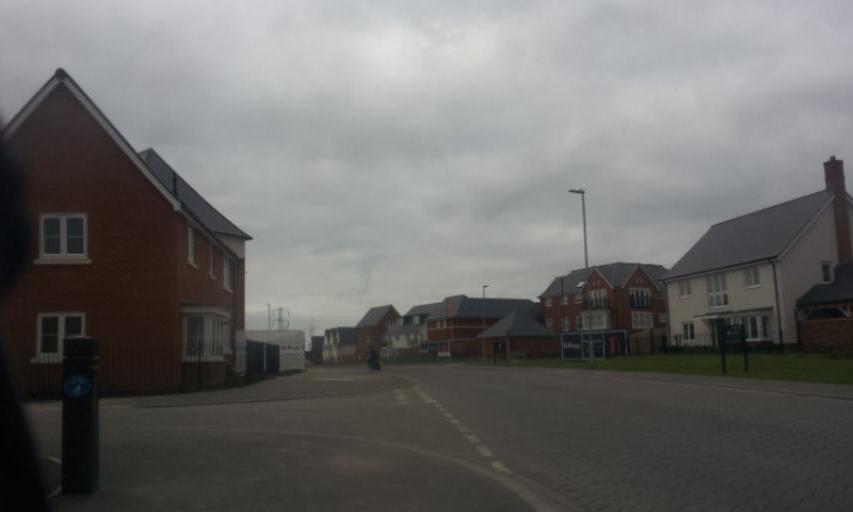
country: GB
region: England
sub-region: Kent
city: Snodland
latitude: 51.3375
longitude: 0.4585
